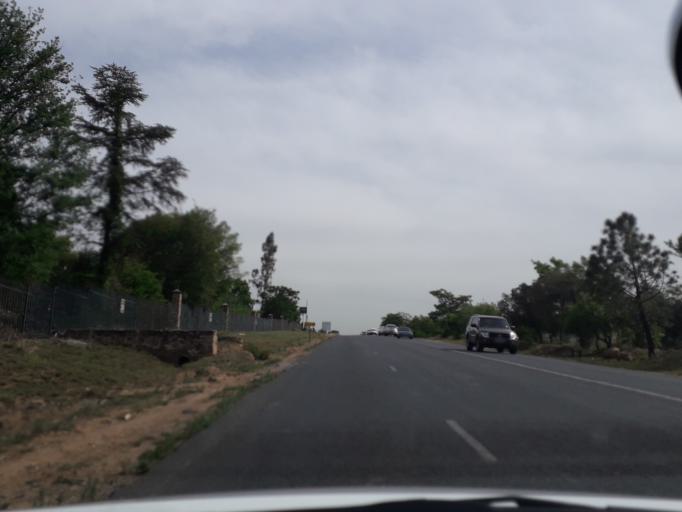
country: ZA
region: Gauteng
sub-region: City of Johannesburg Metropolitan Municipality
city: Diepsloot
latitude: -26.0106
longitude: 28.0374
